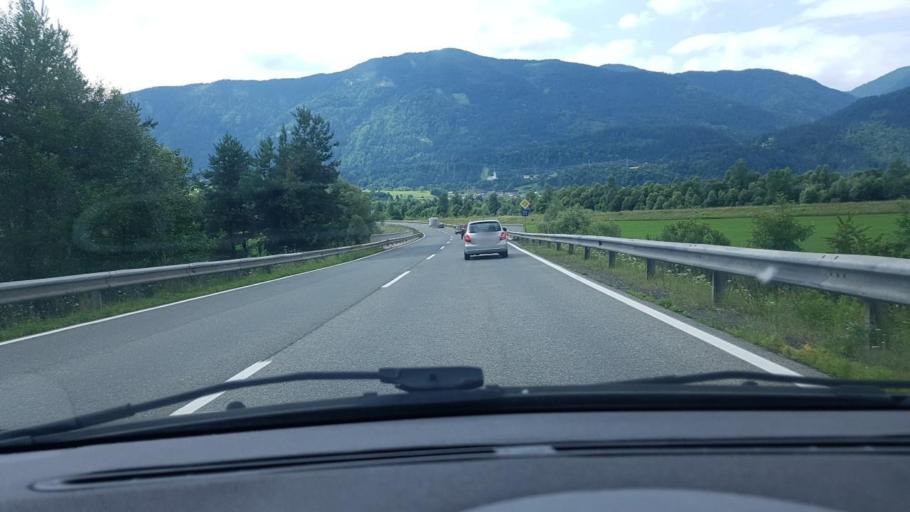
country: AT
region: Carinthia
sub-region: Politischer Bezirk Villach Land
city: Feistritz an der Gail
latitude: 46.5917
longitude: 13.6140
